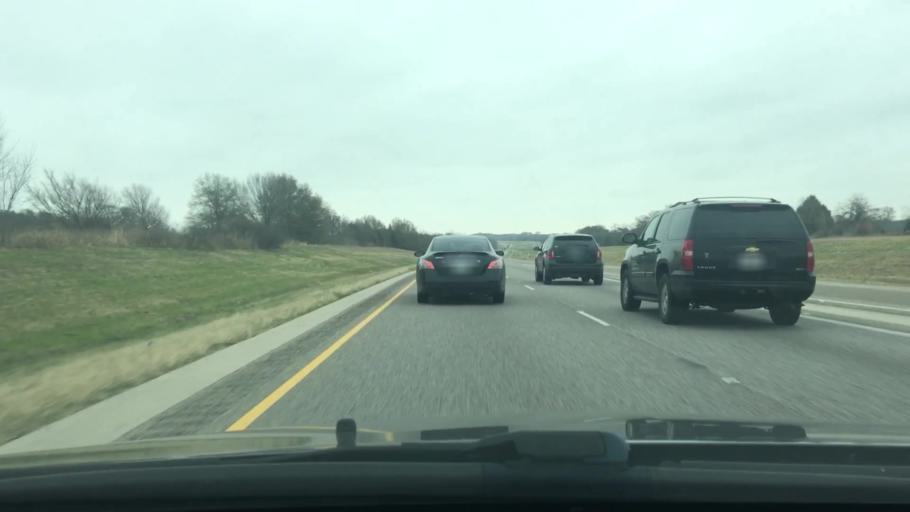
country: US
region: Texas
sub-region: Freestone County
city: Fairfield
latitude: 31.8042
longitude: -96.2627
